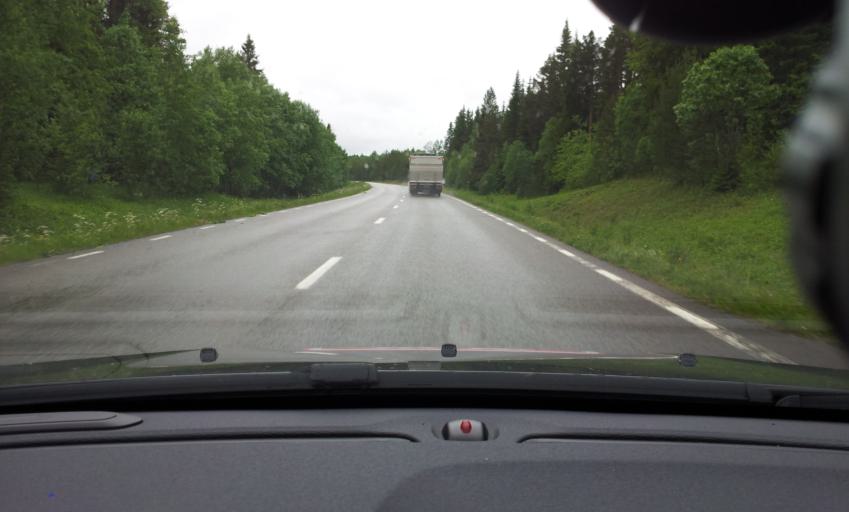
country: SE
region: Jaemtland
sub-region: OEstersunds Kommun
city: Lit
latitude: 63.6573
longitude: 14.6469
